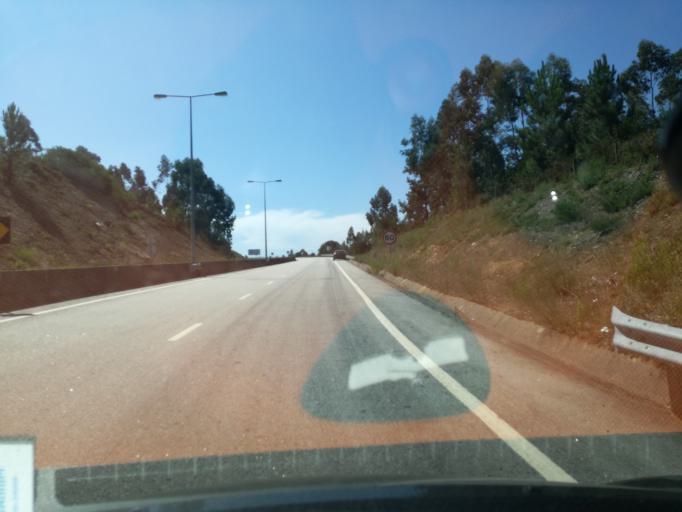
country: ES
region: Galicia
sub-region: Provincia de Pontevedra
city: O Rosal
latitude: 41.8803
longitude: -8.7950
